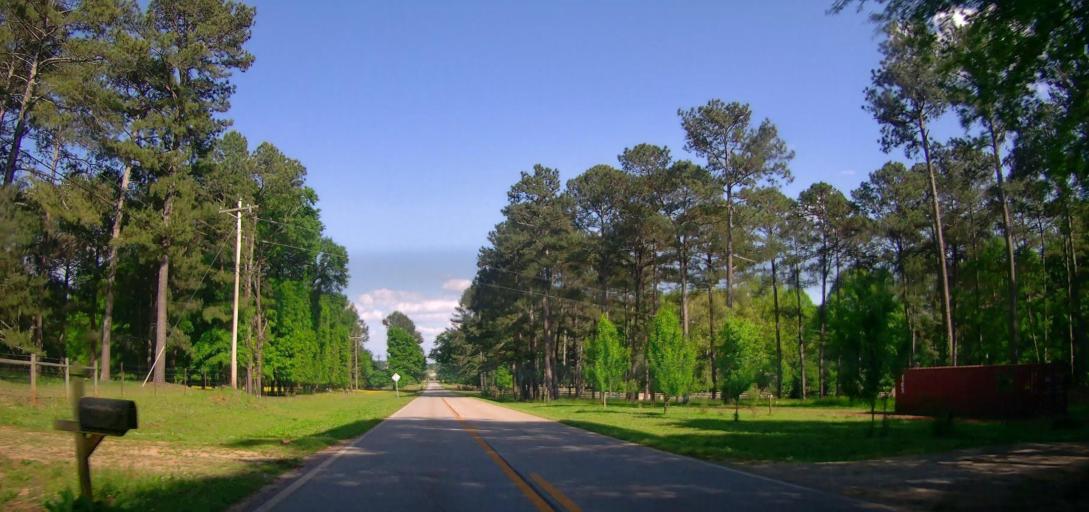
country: US
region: Georgia
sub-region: Morgan County
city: Madison
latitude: 33.6554
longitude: -83.4526
